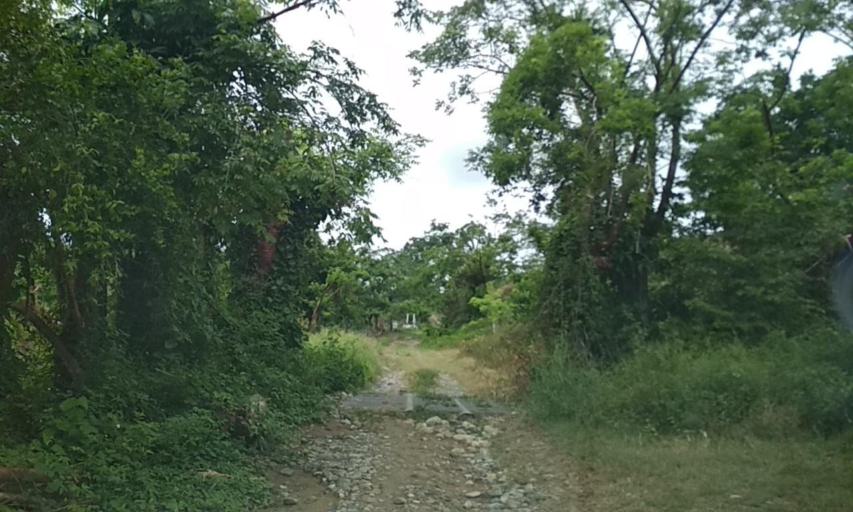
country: MX
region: Veracruz
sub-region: Papantla
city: Residencial Tajin
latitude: 20.6055
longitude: -97.3352
